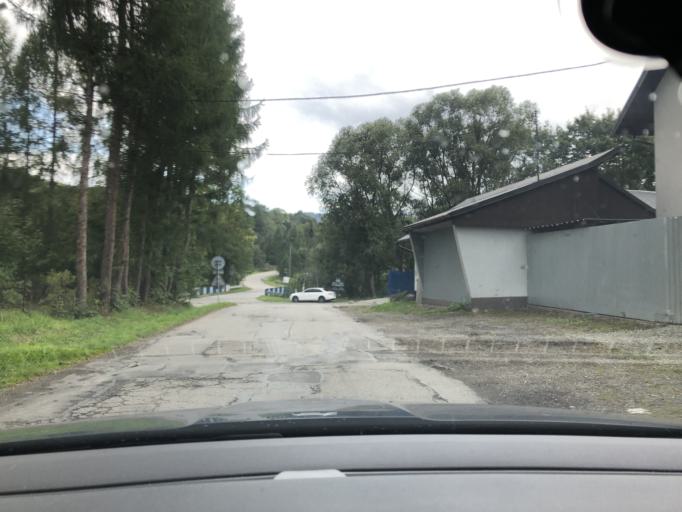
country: PL
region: Silesian Voivodeship
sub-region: Powiat zywiecki
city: Slemien
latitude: 49.7228
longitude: 19.3777
